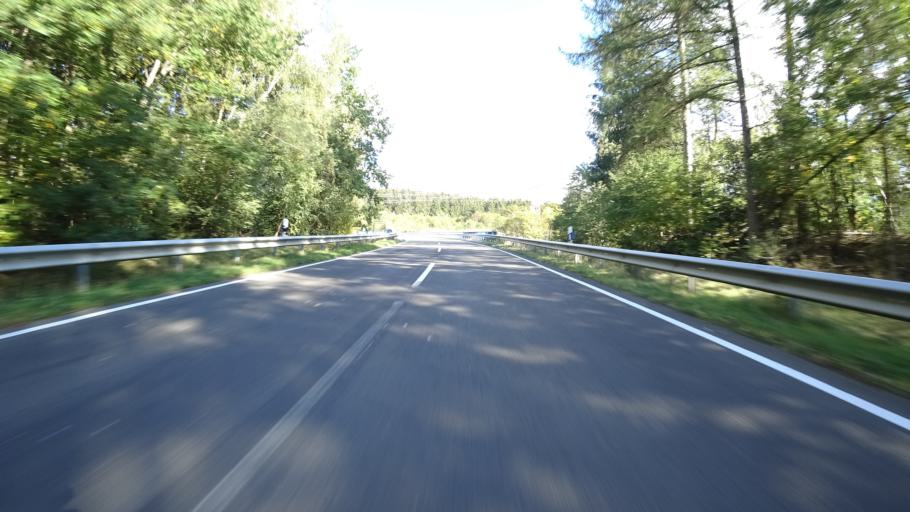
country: DE
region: Rheinland-Pfalz
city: Wiebelsheim
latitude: 50.0643
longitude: 7.6312
